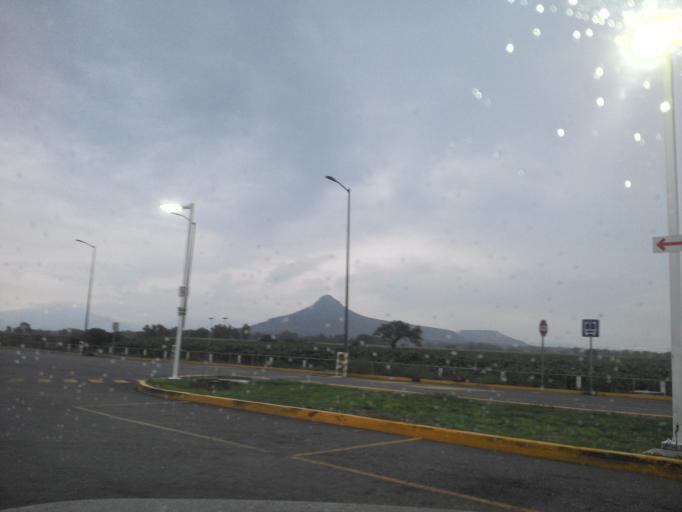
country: MX
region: Hidalgo
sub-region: Tula de Allende
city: Residencial Arboledas
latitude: 20.0953
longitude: -99.2994
